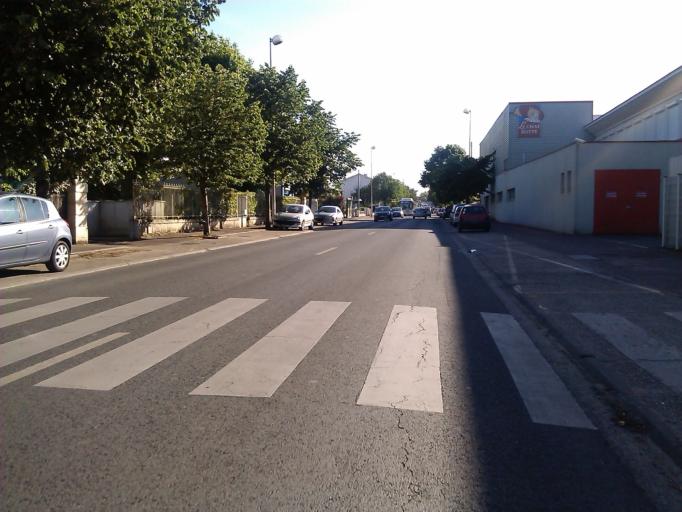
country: FR
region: Aquitaine
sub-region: Departement de la Gironde
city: Pessac
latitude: 44.8097
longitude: -0.6223
